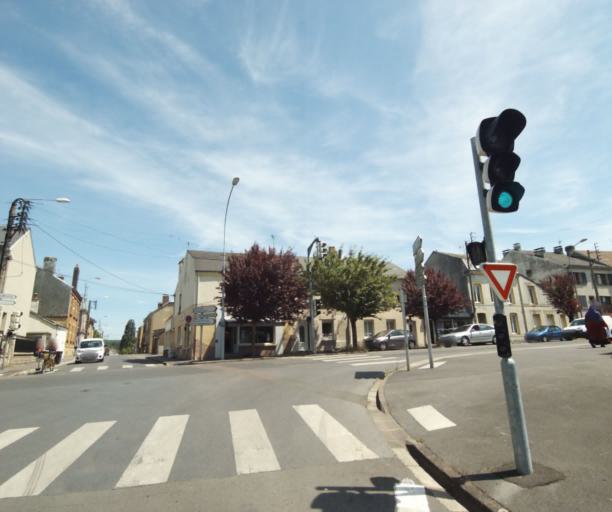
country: FR
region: Champagne-Ardenne
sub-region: Departement des Ardennes
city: Charleville-Mezieres
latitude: 49.7509
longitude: 4.7241
